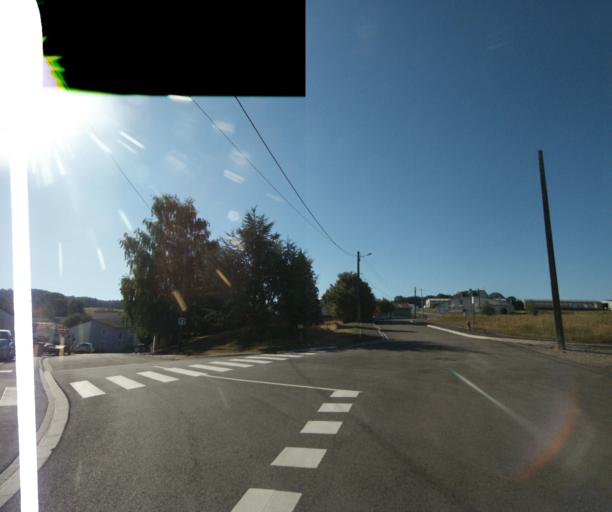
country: FR
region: Lorraine
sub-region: Departement des Vosges
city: Epinal
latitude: 48.1752
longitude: 6.4684
